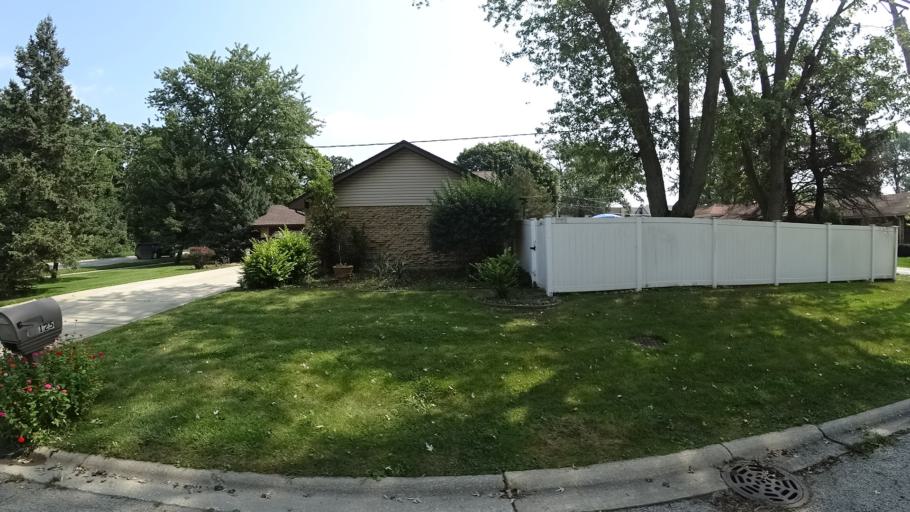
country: US
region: Illinois
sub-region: Cook County
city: Orland Park
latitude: 41.6298
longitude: -87.8670
